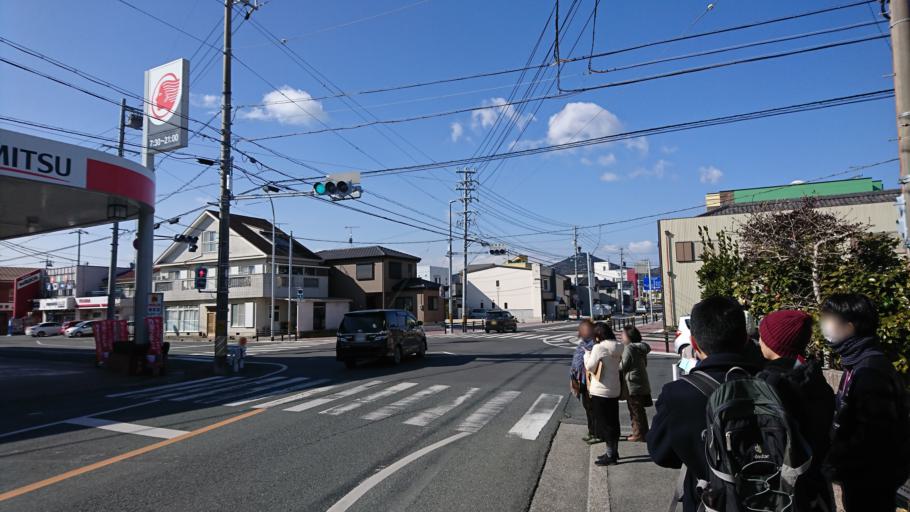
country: JP
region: Aichi
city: Tahara
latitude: 34.6683
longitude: 137.2716
